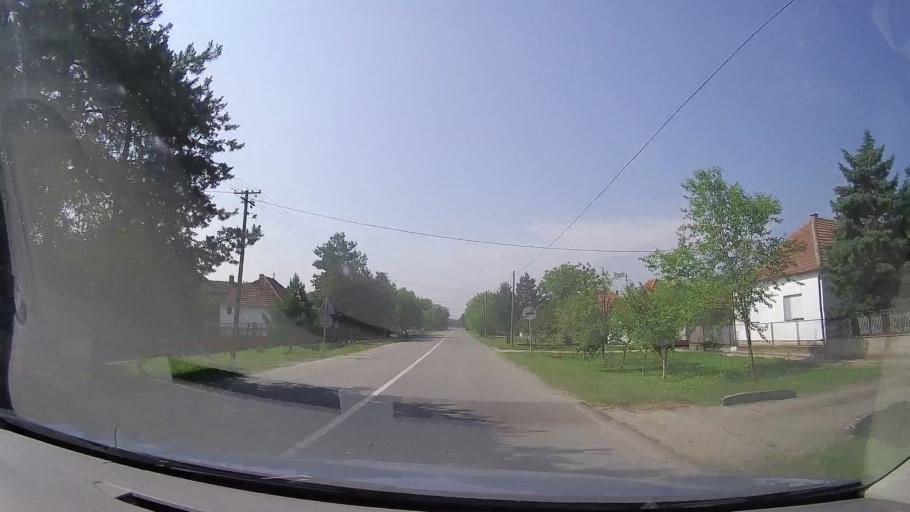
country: RS
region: Autonomna Pokrajina Vojvodina
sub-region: Srednjebanatski Okrug
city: Secanj
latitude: 45.3734
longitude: 20.7779
